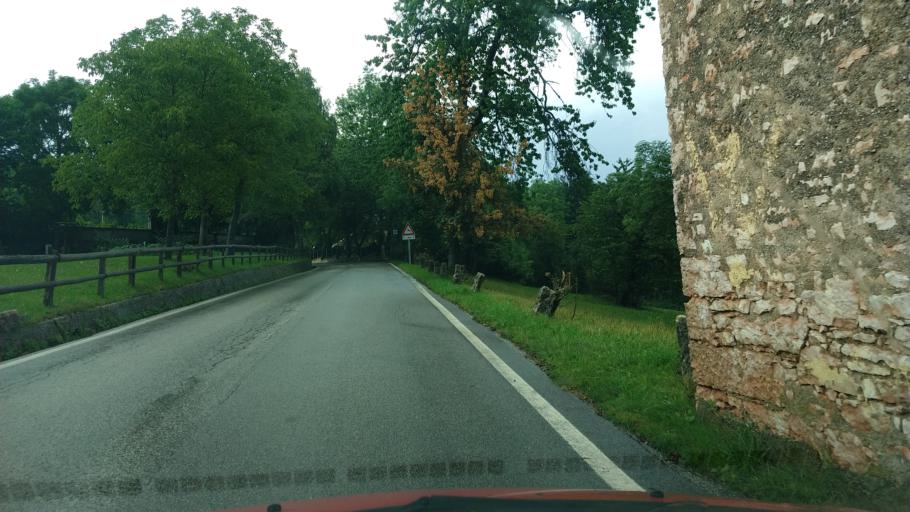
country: IT
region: Veneto
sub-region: Provincia di Vicenza
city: Tonezza del Cimone
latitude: 45.8578
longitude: 11.3375
